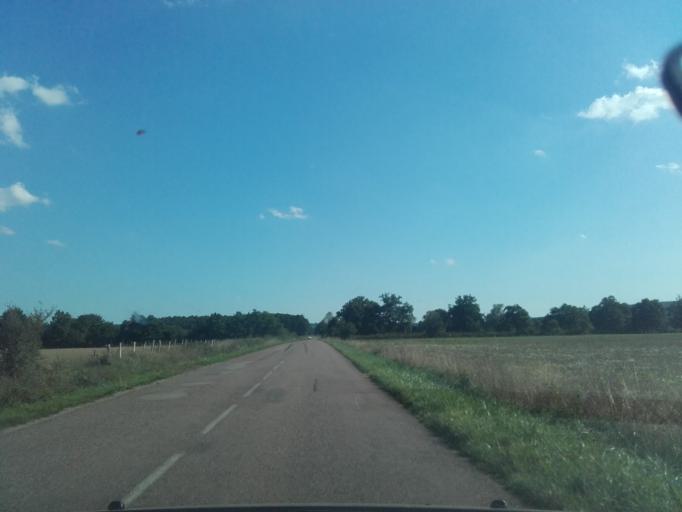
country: FR
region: Bourgogne
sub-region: Departement de Saone-et-Loire
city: Epinac
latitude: 46.9964
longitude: 4.4800
